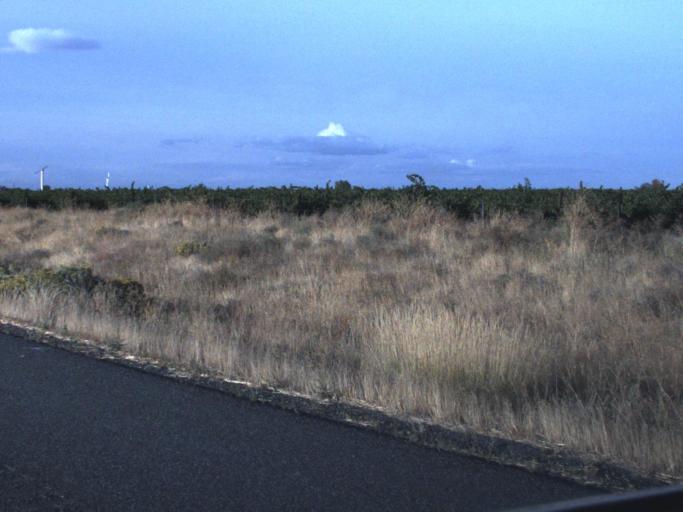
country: US
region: Washington
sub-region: Benton County
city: West Richland
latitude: 46.2354
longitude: -119.3575
